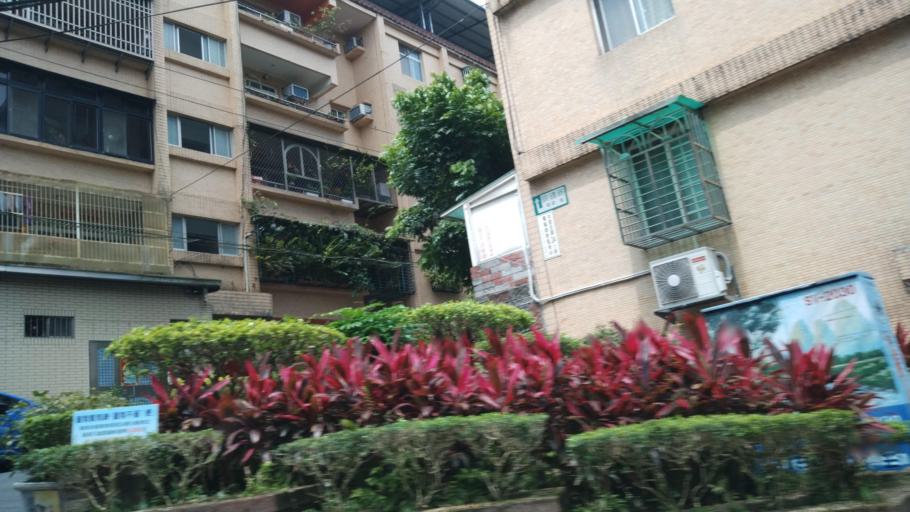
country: TW
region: Taipei
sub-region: Taipei
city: Banqiao
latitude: 24.9461
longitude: 121.4956
